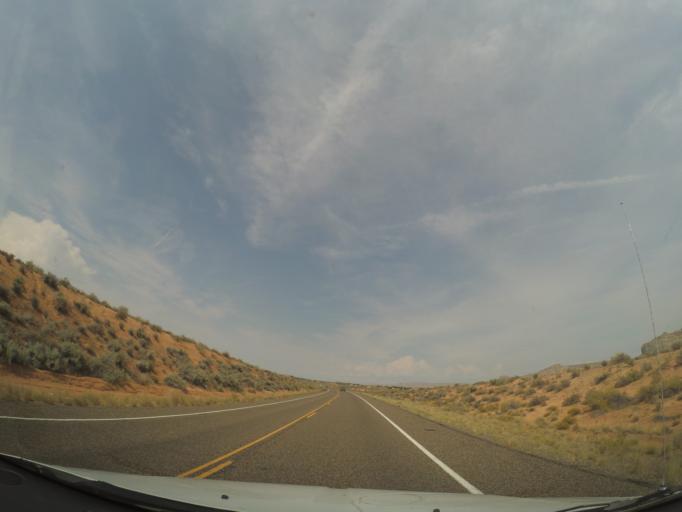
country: US
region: Arizona
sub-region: Coconino County
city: Page
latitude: 37.0504
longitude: -111.6270
